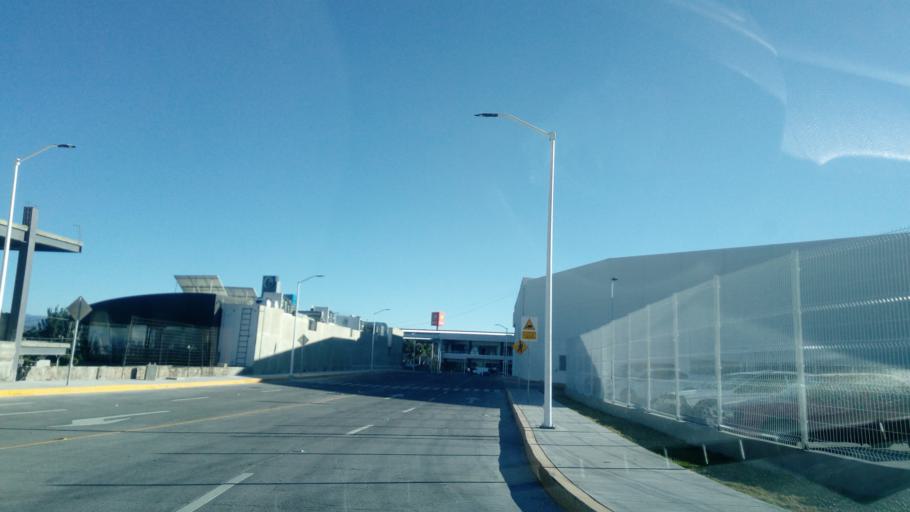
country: MX
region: Durango
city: Victoria de Durango
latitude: 24.0146
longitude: -104.6910
